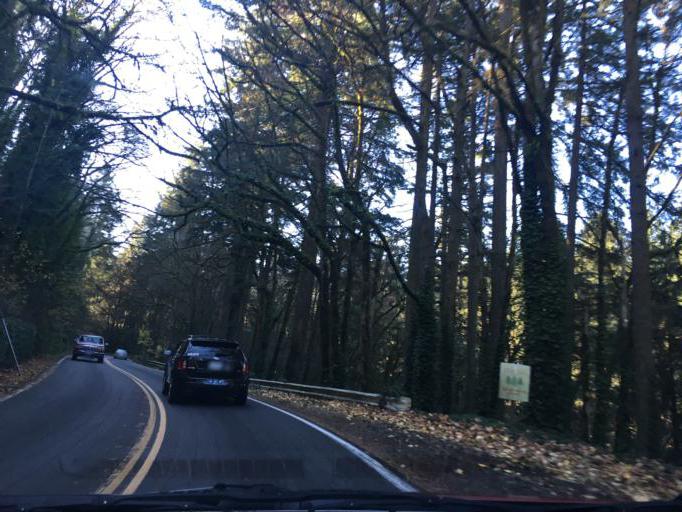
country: US
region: Oregon
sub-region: Washington County
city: Cedar Mill
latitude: 45.5905
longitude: -122.7831
